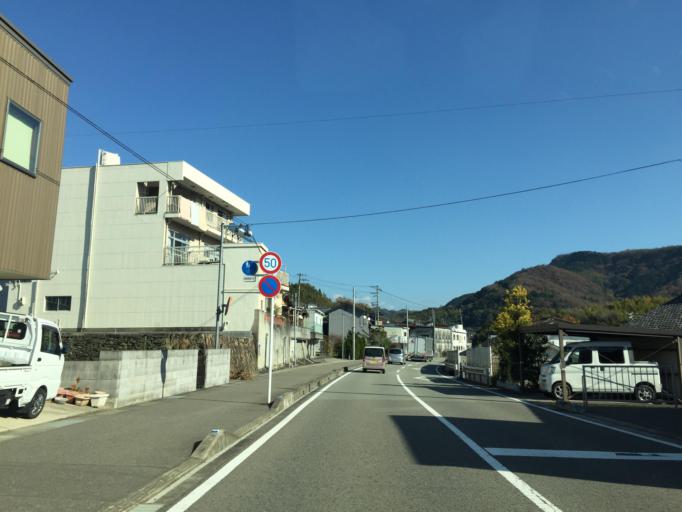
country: JP
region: Wakayama
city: Iwade
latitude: 34.1649
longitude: 135.2984
